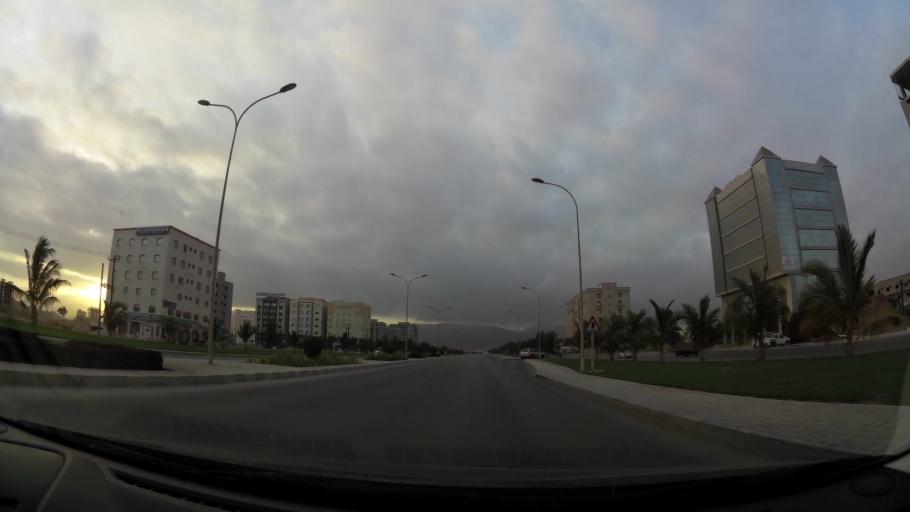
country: OM
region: Zufar
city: Salalah
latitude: 17.0227
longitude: 54.0334
